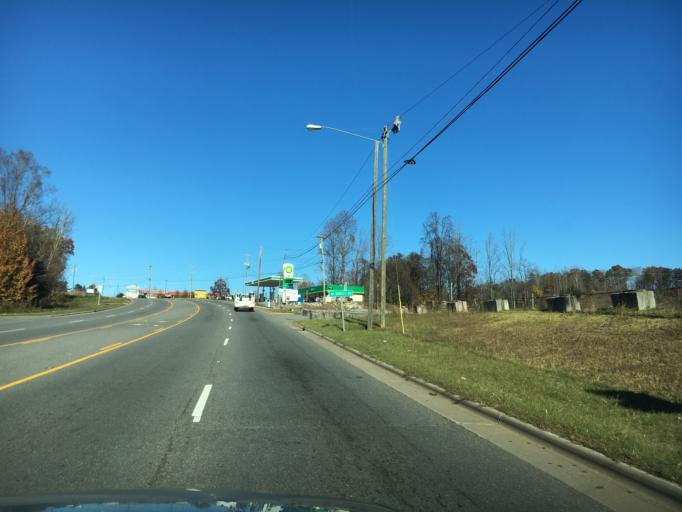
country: US
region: North Carolina
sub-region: McDowell County
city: West Marion
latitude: 35.6478
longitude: -82.0341
